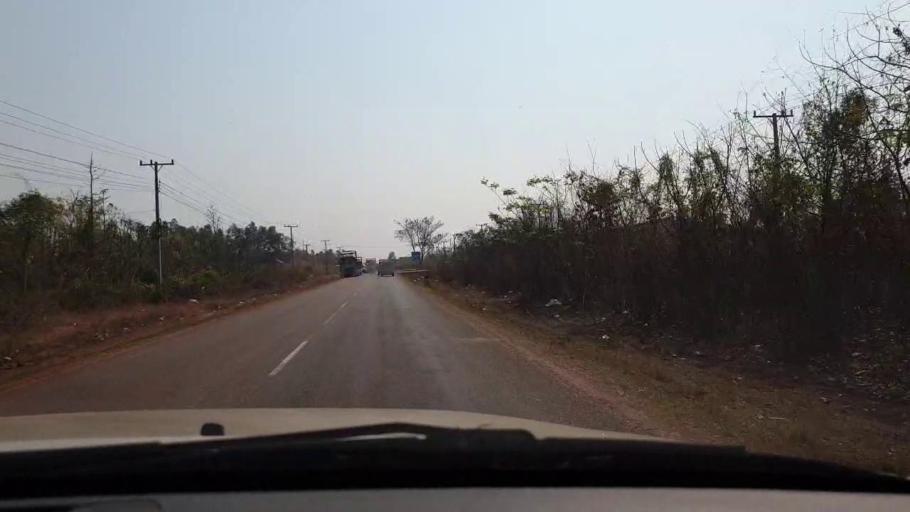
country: TH
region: Nong Khai
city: Nong Khai
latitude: 18.0535
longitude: 102.8415
